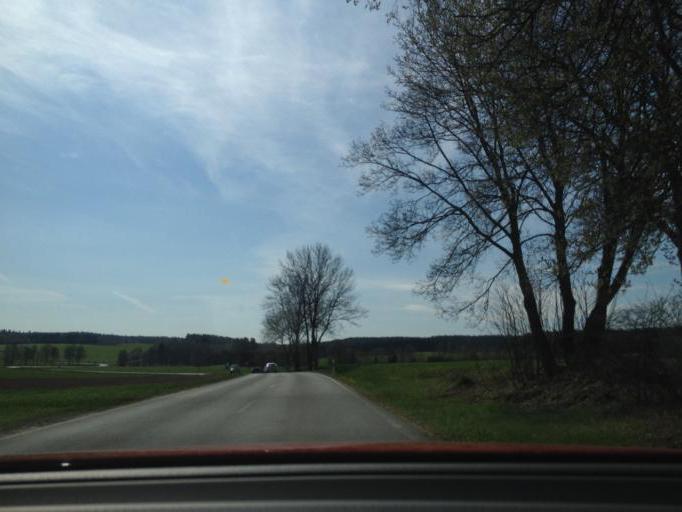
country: DE
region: Bavaria
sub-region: Upper Franconia
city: Weissenstadt
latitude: 50.0953
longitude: 11.8924
